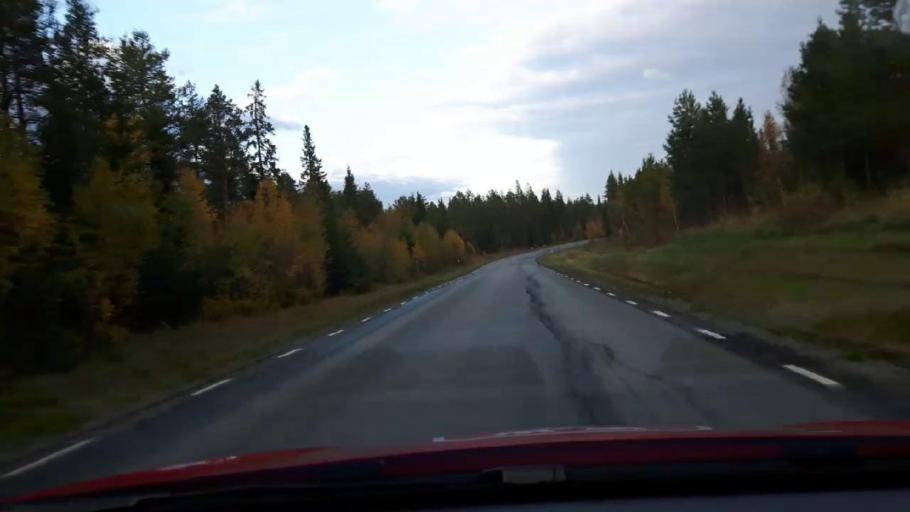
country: SE
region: Jaemtland
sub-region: OEstersunds Kommun
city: Lit
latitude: 63.3159
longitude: 15.0328
